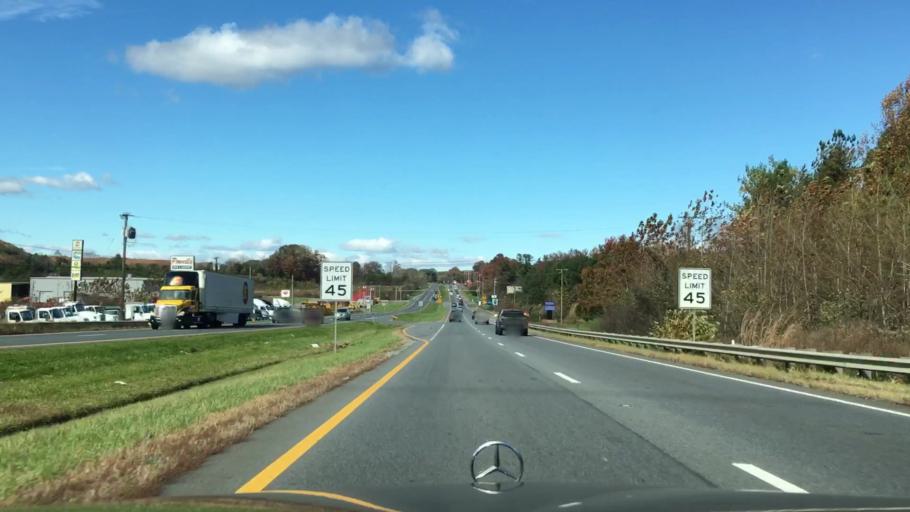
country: US
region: Virginia
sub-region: Campbell County
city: Timberlake
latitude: 37.3087
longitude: -79.1813
